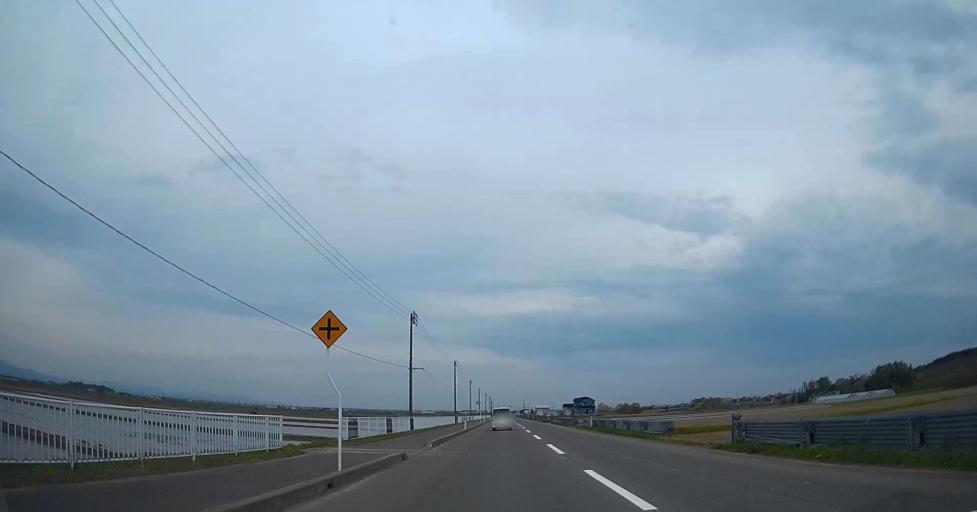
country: JP
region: Aomori
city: Goshogawara
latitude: 40.8986
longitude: 140.4724
